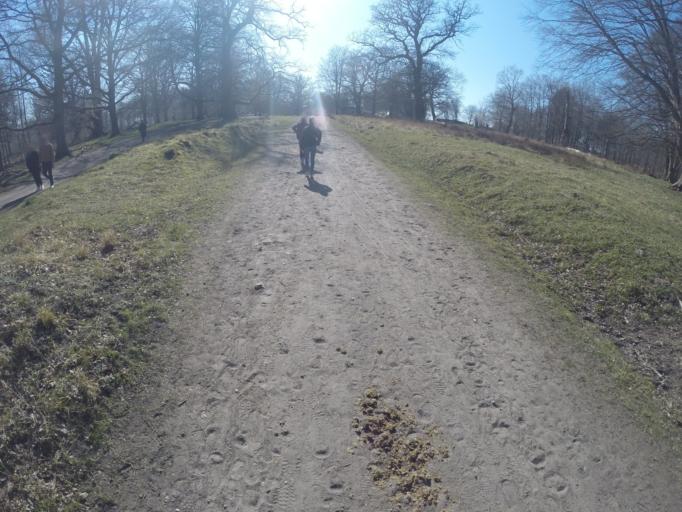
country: DK
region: Capital Region
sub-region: Lyngby-Tarbaek Kommune
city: Kongens Lyngby
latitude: 55.7767
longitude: 12.5466
